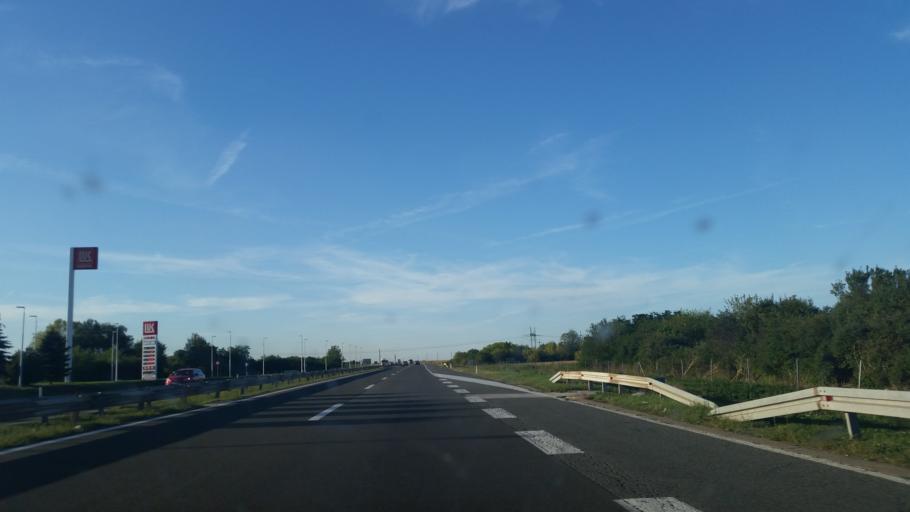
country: RS
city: Lugavcina
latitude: 44.5519
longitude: 20.9850
